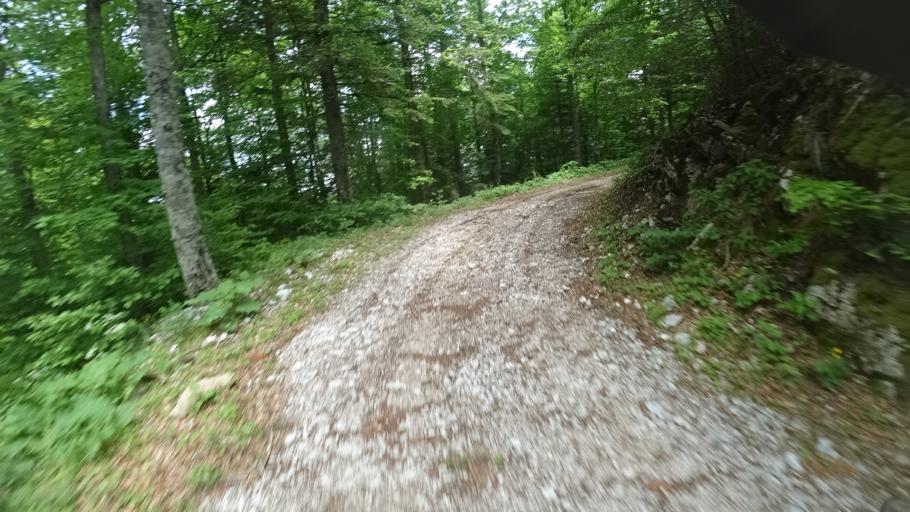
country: HR
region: Zadarska
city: Gracac
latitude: 44.4797
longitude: 15.8895
